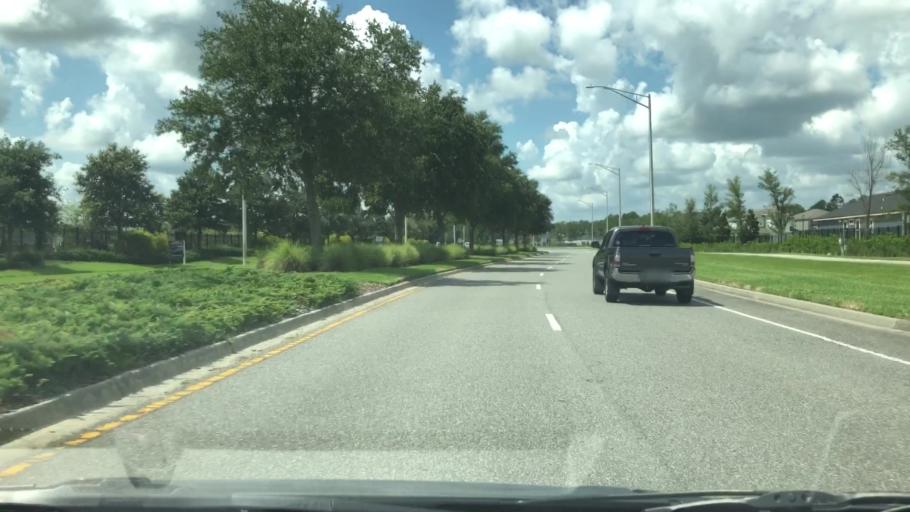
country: US
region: Florida
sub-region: Saint Johns County
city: Fruit Cove
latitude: 30.1095
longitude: -81.5186
